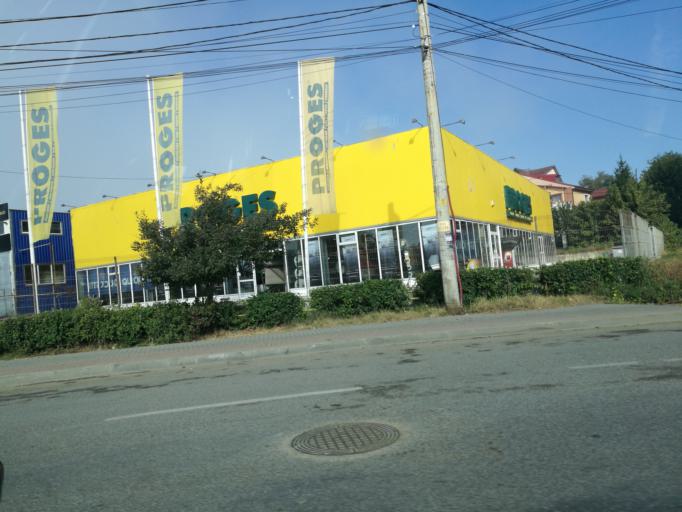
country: RO
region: Iasi
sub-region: Comuna Miroslava
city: Miroslava
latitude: 47.1731
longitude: 27.5325
